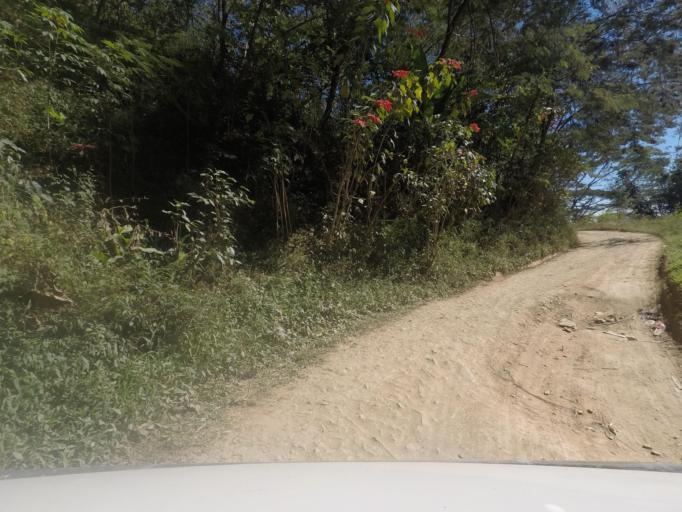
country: TL
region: Ermera
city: Gleno
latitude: -8.7409
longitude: 125.3471
